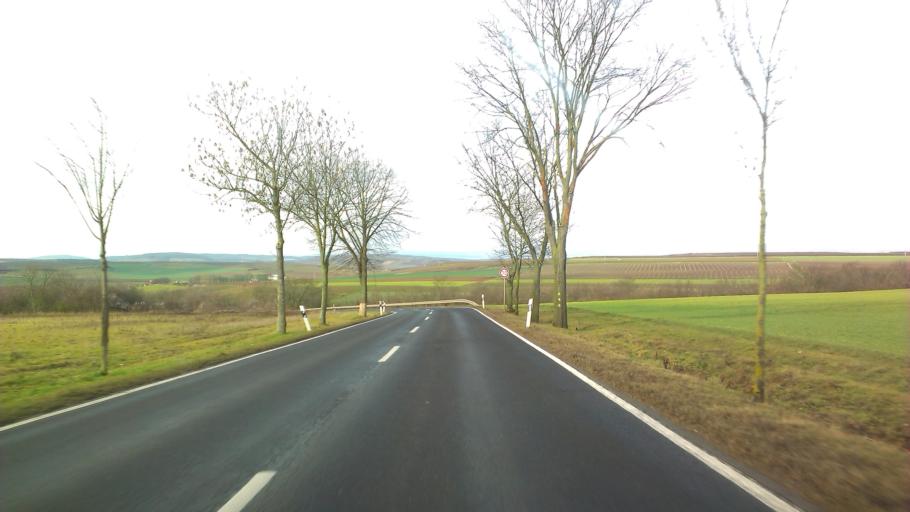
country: DE
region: Rheinland-Pfalz
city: Wendelsheim
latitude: 49.7668
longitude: 8.0145
